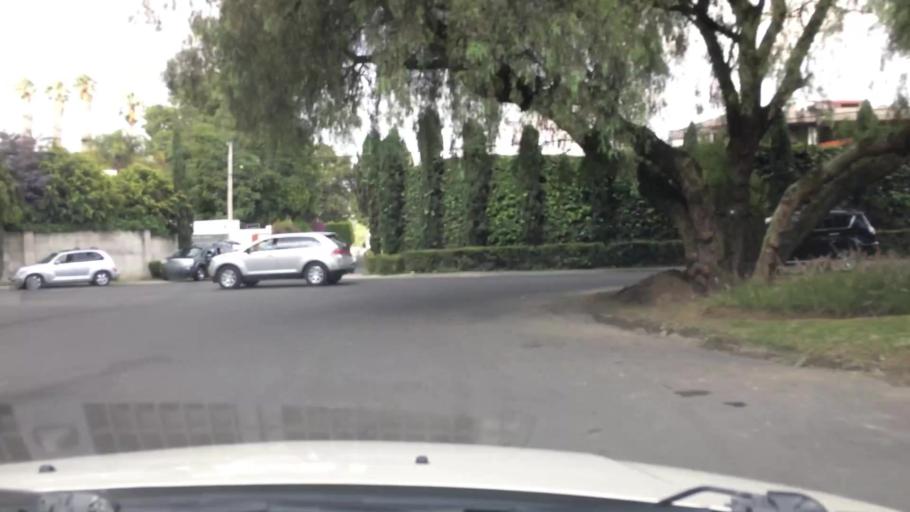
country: MX
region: Mexico City
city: Magdalena Contreras
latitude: 19.3107
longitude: -99.2102
